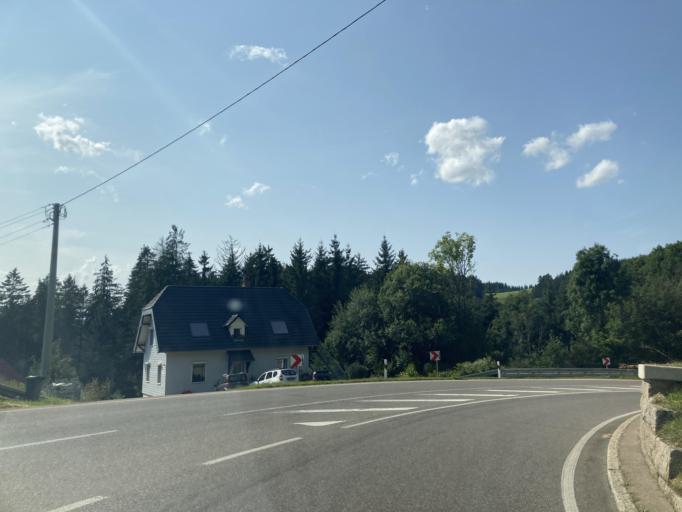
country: DE
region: Baden-Wuerttemberg
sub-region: Freiburg Region
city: Triberg im Schwarzwald
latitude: 48.1348
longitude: 8.2787
